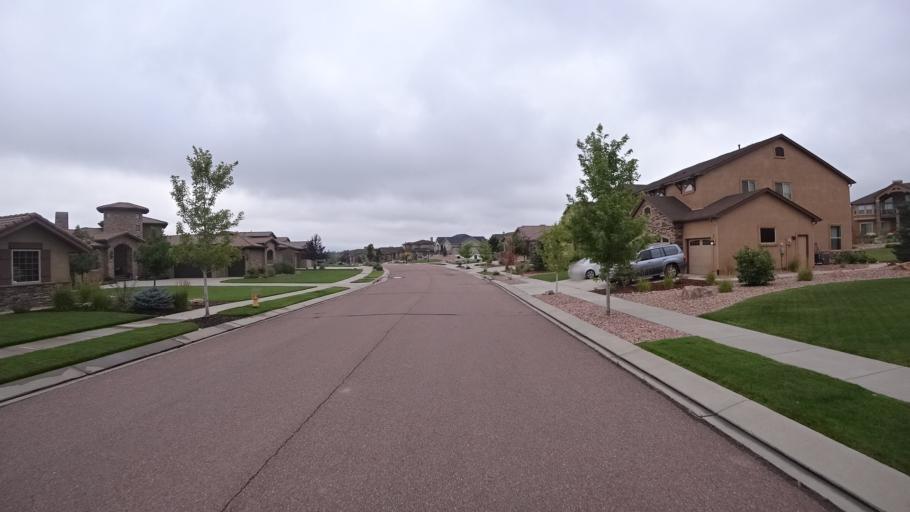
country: US
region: Colorado
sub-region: El Paso County
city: Gleneagle
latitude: 39.0257
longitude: -104.7889
